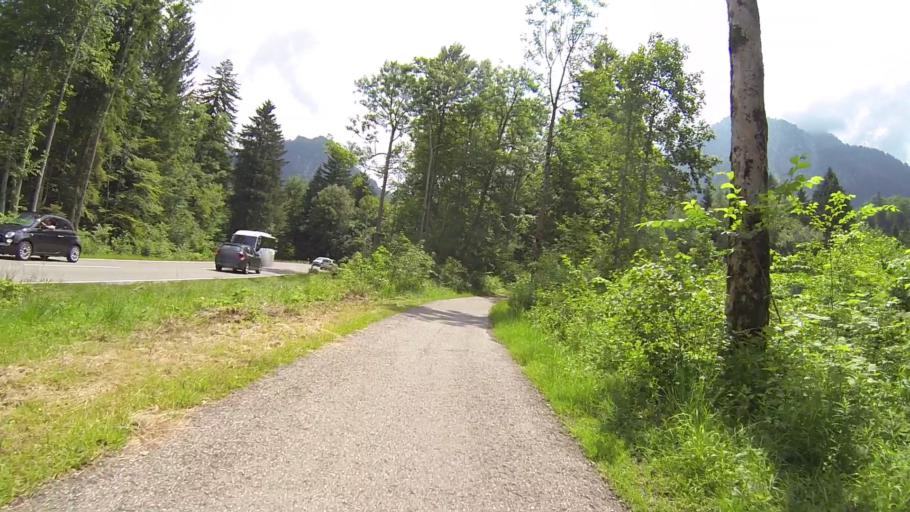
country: DE
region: Bavaria
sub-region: Swabia
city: Schwangau
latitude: 47.5588
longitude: 10.7330
